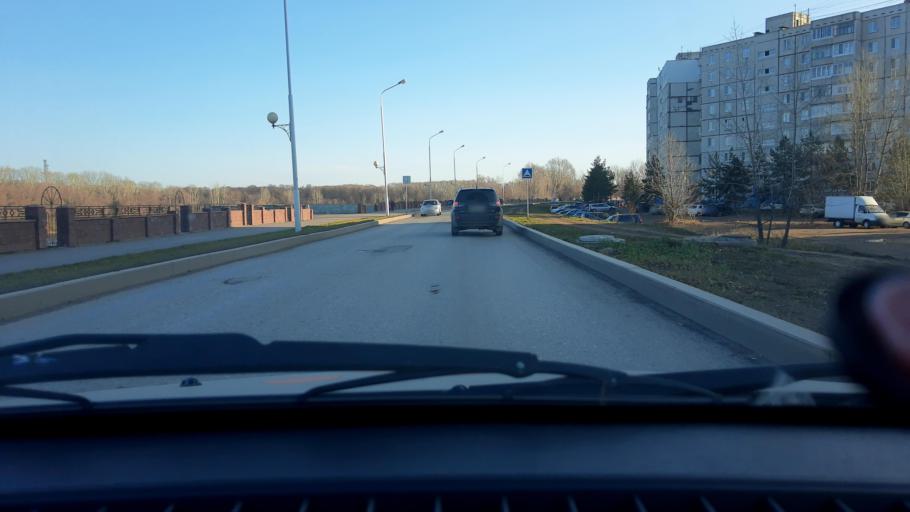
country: RU
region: Bashkortostan
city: Ufa
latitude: 54.7768
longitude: 56.0824
